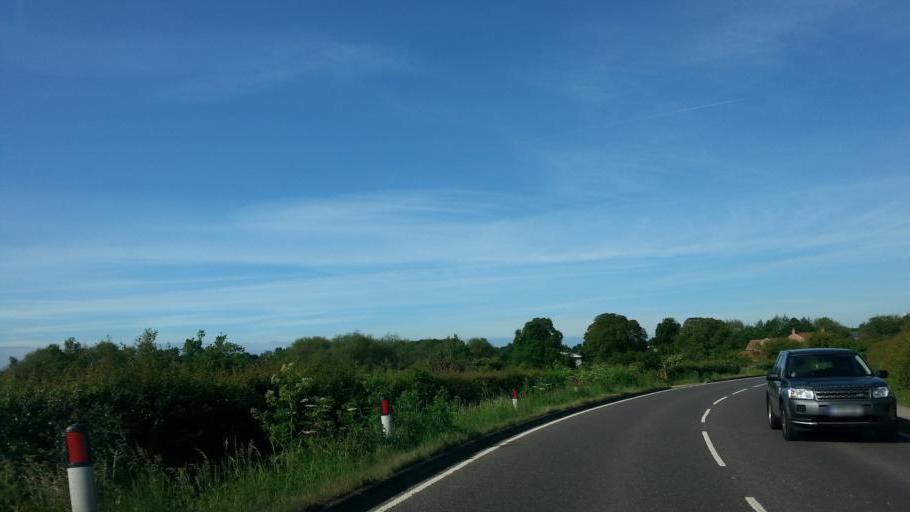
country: GB
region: England
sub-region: Nottinghamshire
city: Southwell
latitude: 53.0797
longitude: -0.9349
